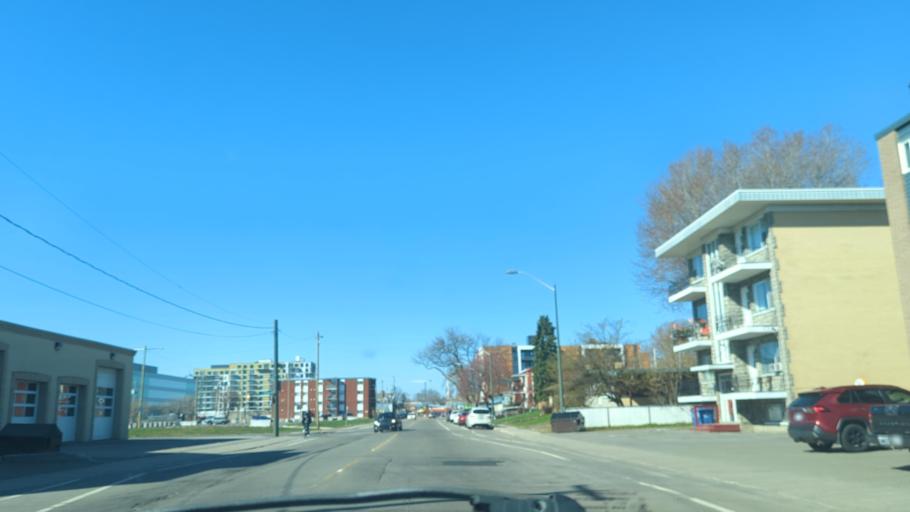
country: CA
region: Quebec
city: Quebec
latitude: 46.8479
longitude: -71.2123
